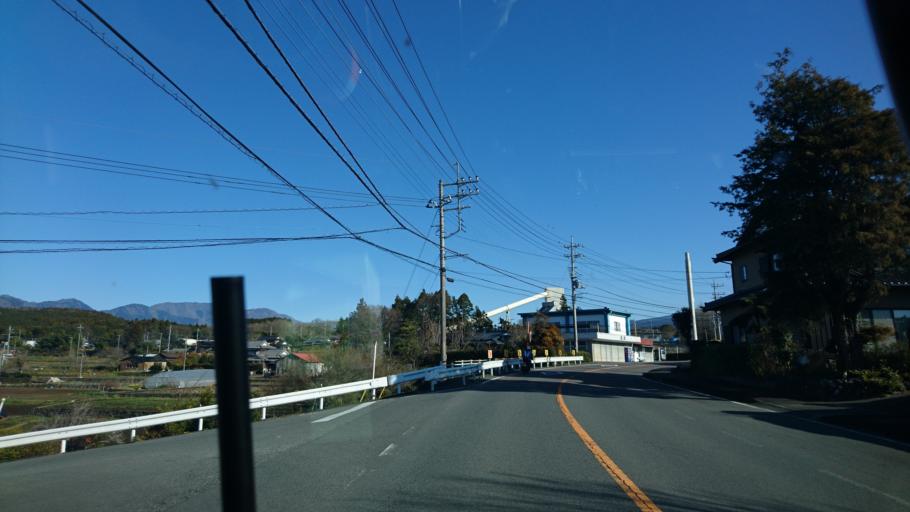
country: JP
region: Shizuoka
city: Fujinomiya
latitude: 35.2730
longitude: 138.6022
